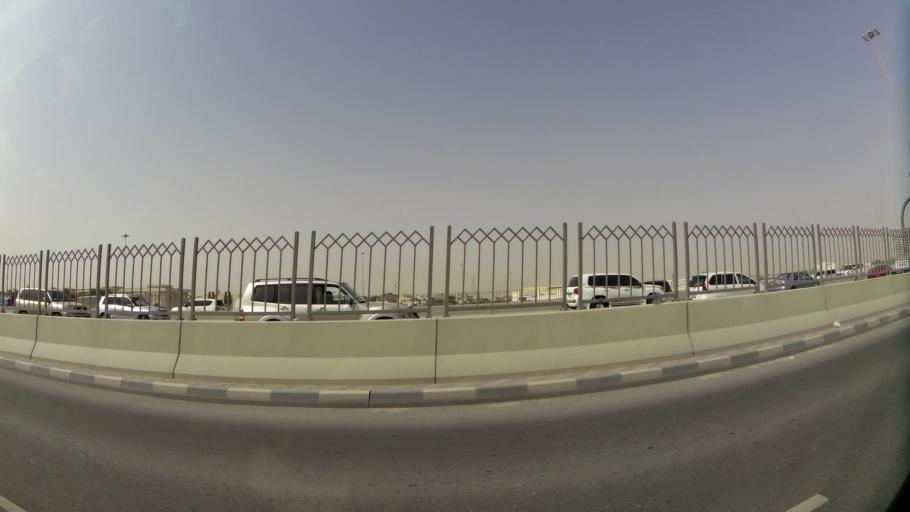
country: QA
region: Baladiyat ad Dawhah
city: Doha
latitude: 25.2810
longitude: 51.4856
